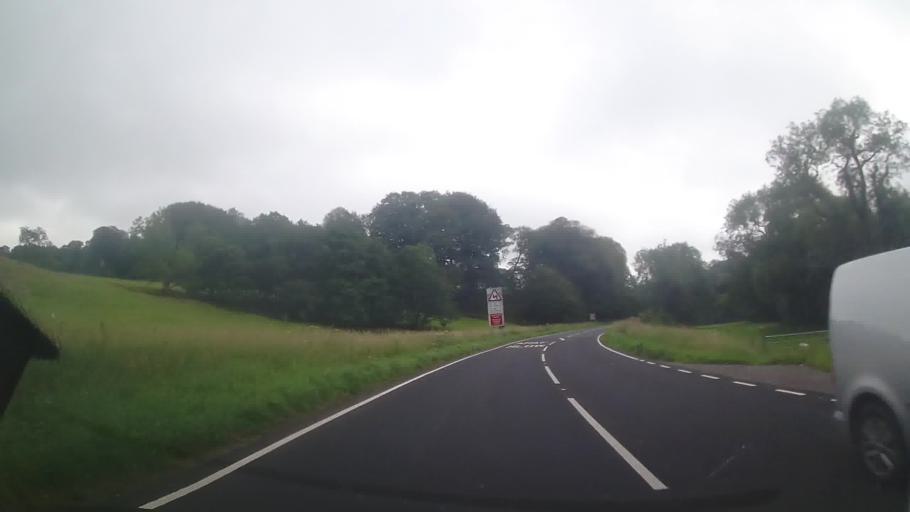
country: GB
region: Wales
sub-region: Conwy
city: Betws-y-Coed
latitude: 53.0547
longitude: -3.7440
